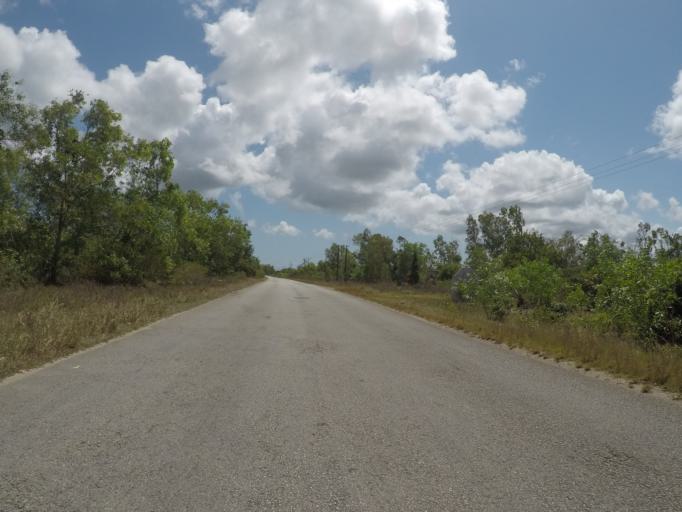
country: TZ
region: Zanzibar Central/South
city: Nganane
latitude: -6.2860
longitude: 39.4512
